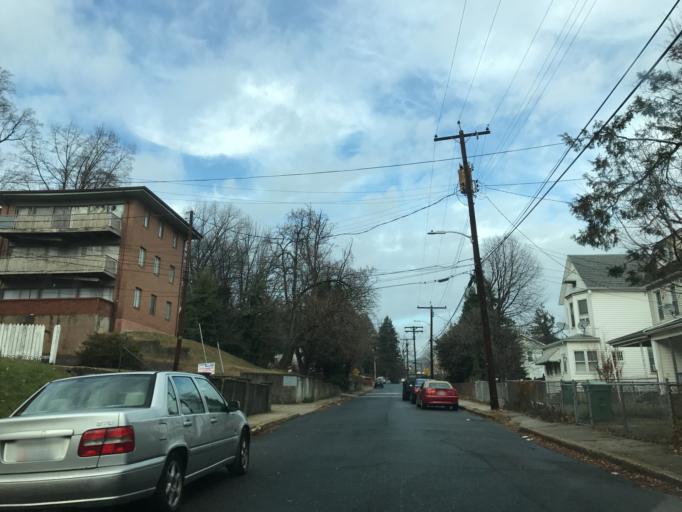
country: US
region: Maryland
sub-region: Baltimore County
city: Overlea
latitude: 39.3492
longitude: -76.5382
